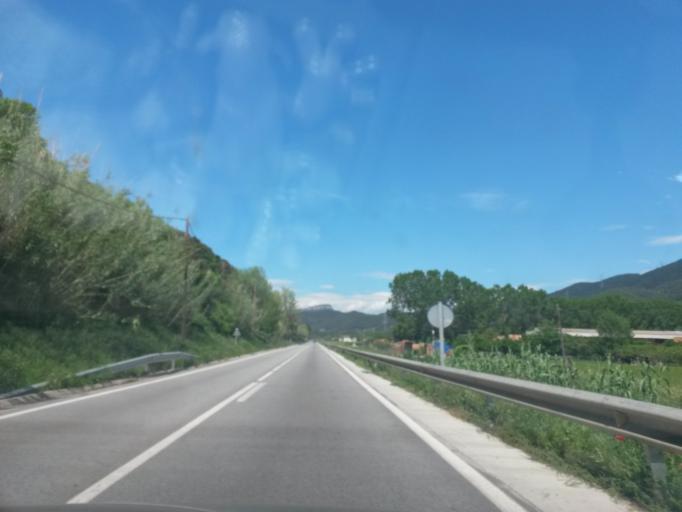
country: ES
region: Catalonia
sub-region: Provincia de Girona
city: Sant Gregori
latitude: 41.9700
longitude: 2.7184
